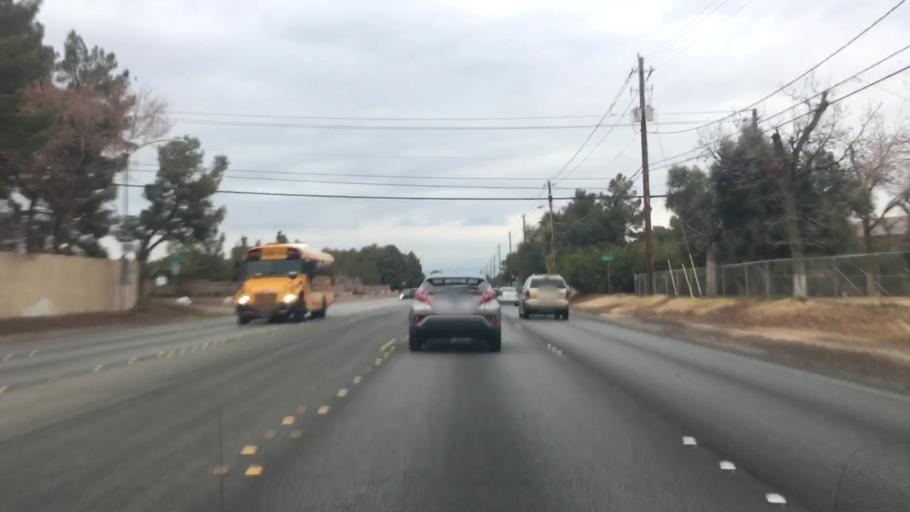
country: US
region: Nevada
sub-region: Clark County
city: Whitney
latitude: 36.0638
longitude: -115.1005
